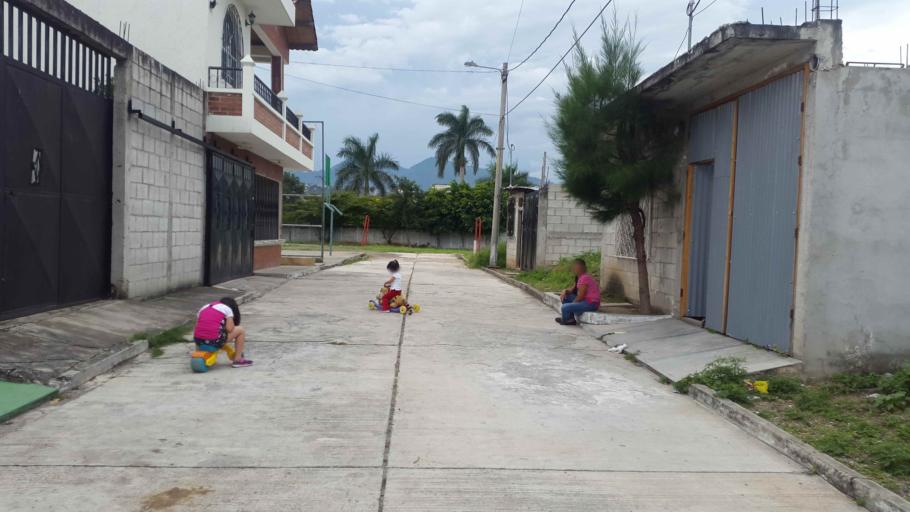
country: GT
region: Guatemala
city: Petapa
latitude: 14.4999
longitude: -90.5652
